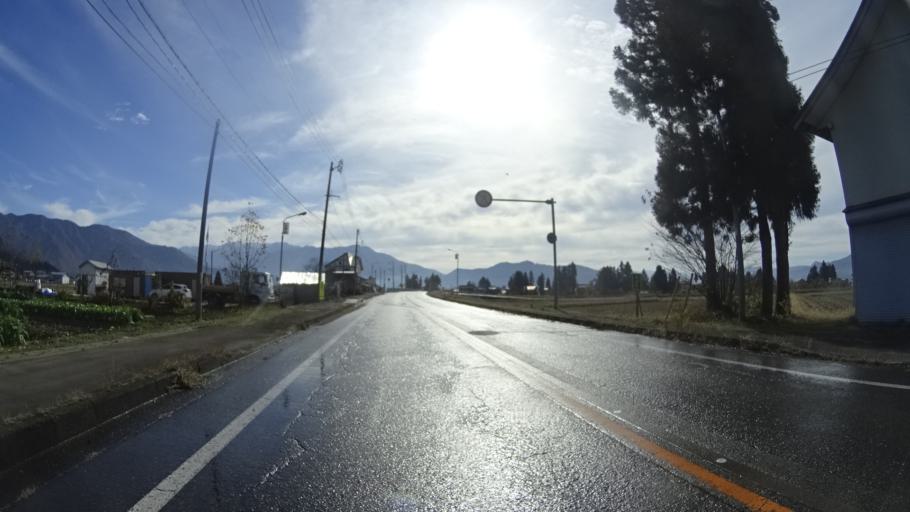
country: JP
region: Niigata
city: Muikamachi
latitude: 37.1071
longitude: 138.9211
